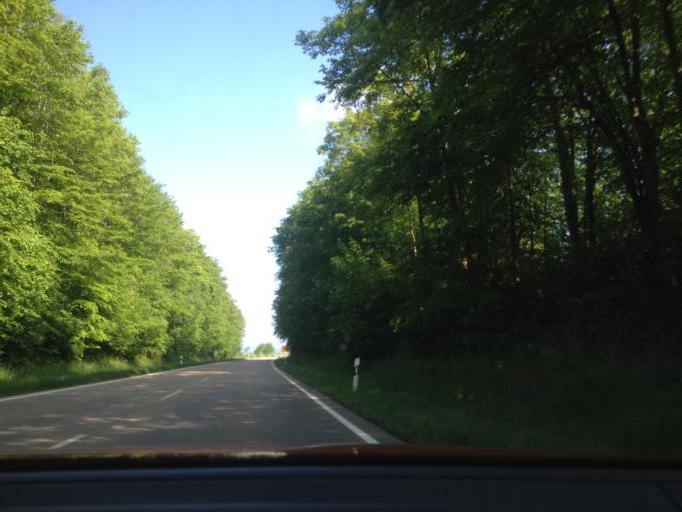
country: DE
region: Bavaria
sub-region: Upper Palatinate
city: Kemnath
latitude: 49.8572
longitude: 11.8812
